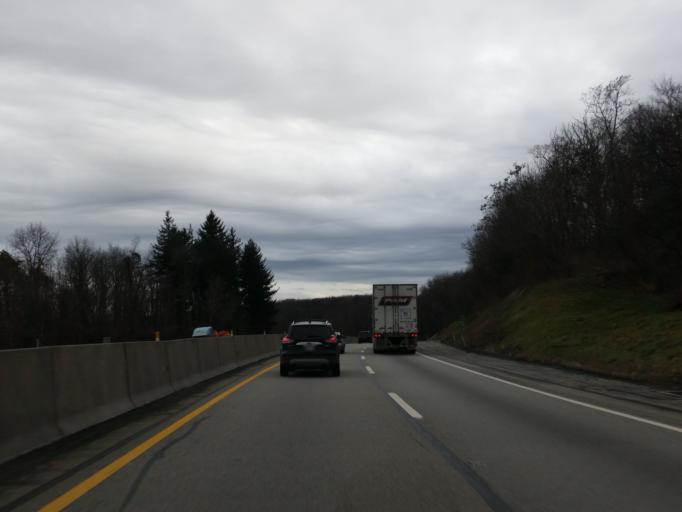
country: US
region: Pennsylvania
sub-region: Somerset County
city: Somerset
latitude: 40.0629
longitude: -79.1412
